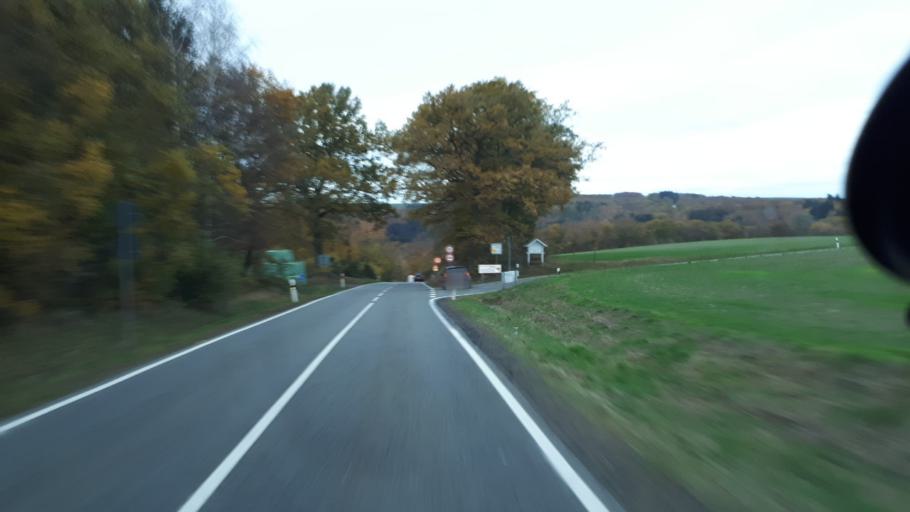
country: DE
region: Rheinland-Pfalz
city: Leienkaul
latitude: 50.2062
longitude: 7.0977
